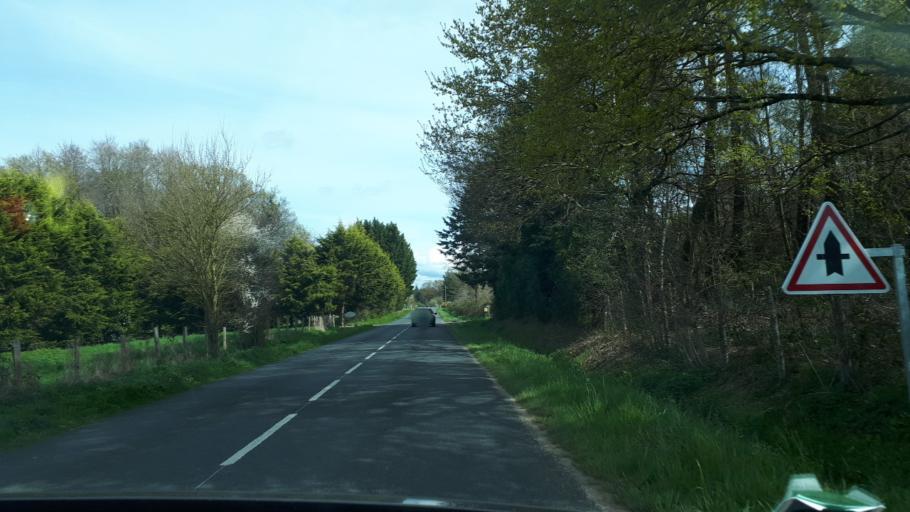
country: FR
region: Pays de la Loire
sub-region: Departement de la Sarthe
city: Ecommoy
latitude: 47.8497
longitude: 0.2872
